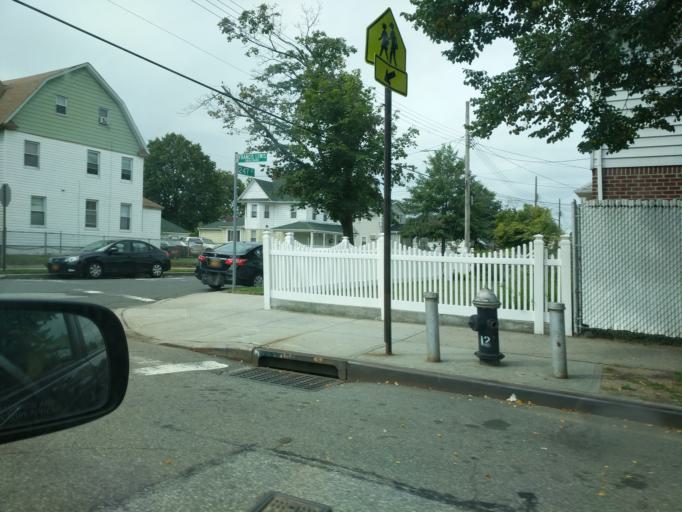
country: US
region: New York
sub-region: Nassau County
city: South Valley Stream
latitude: 40.6639
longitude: -73.7341
